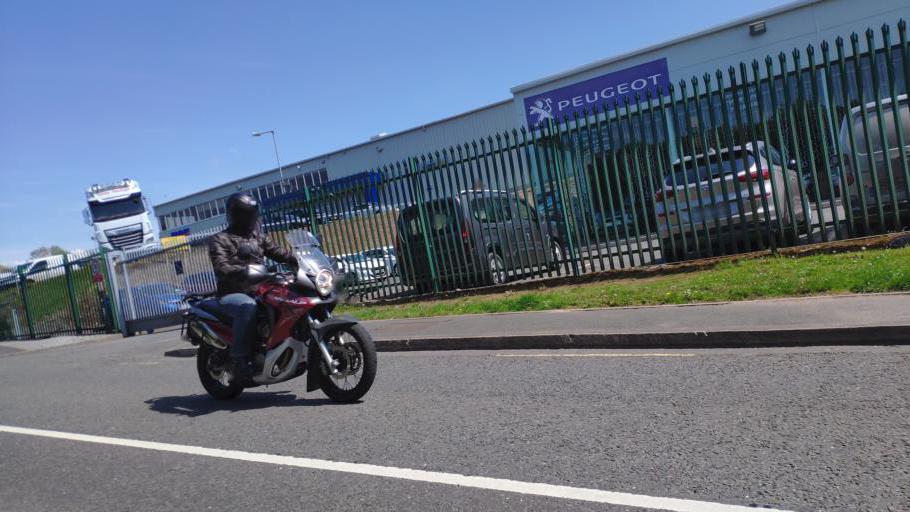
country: IE
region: Munster
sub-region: County Cork
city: Cork
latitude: 51.9273
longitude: -8.4899
